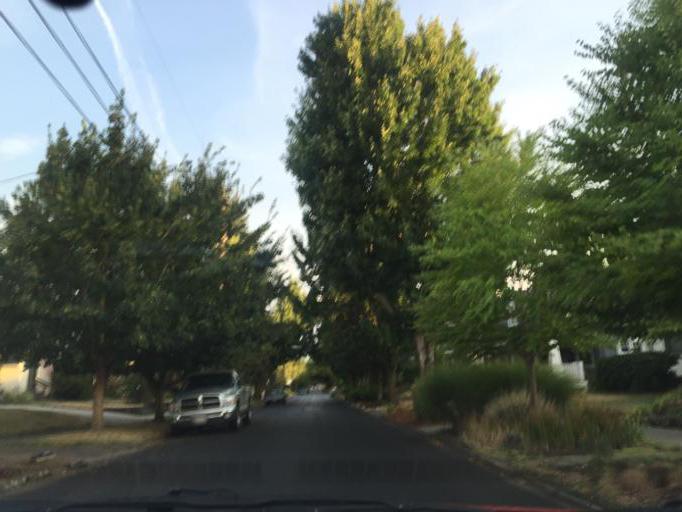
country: US
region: Oregon
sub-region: Multnomah County
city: Portland
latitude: 45.5390
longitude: -122.6240
